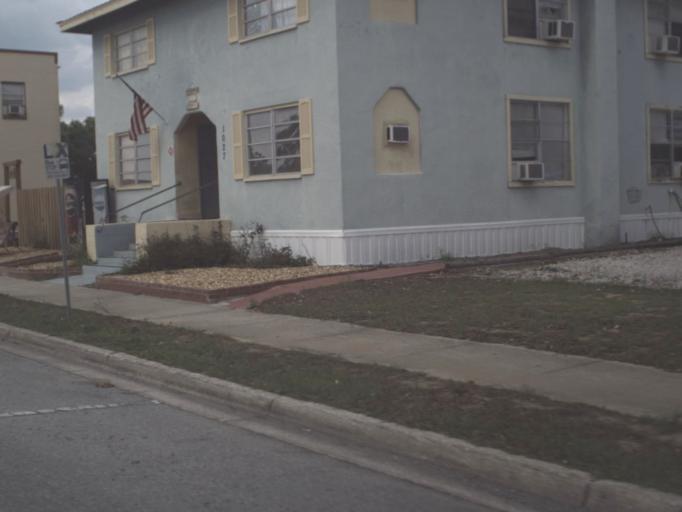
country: US
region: Florida
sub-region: Lake County
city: Eustis
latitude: 28.8430
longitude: -81.6854
